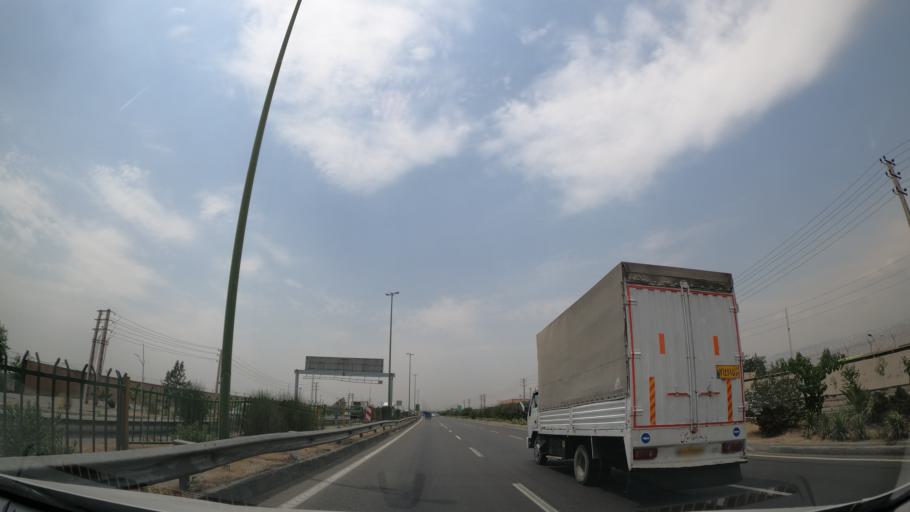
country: IR
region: Tehran
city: Shahr-e Qods
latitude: 35.6970
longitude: 51.1997
